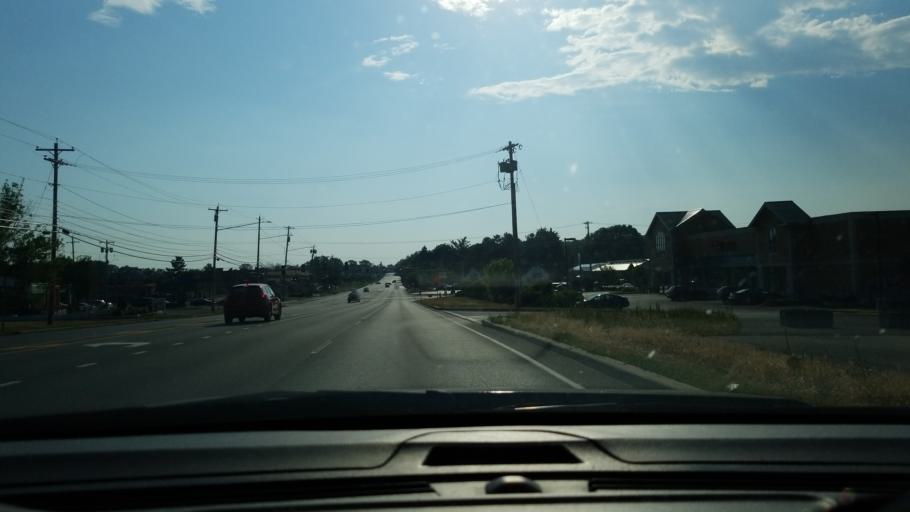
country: US
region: New York
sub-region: Onondaga County
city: Mattydale
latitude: 43.1220
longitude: -76.1579
